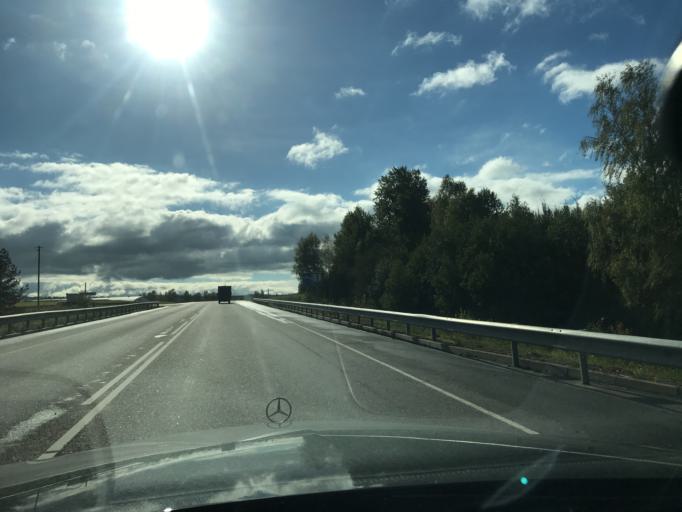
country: EE
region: Vorumaa
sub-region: Voru linn
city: Voru
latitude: 57.8190
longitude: 27.0643
